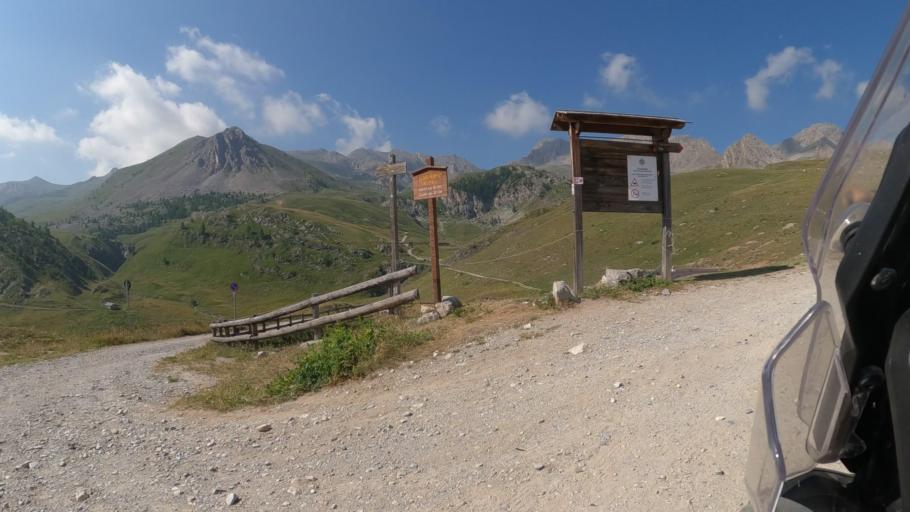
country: IT
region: Piedmont
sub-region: Provincia di Cuneo
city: Pietraporzio
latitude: 44.4043
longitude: 7.0415
